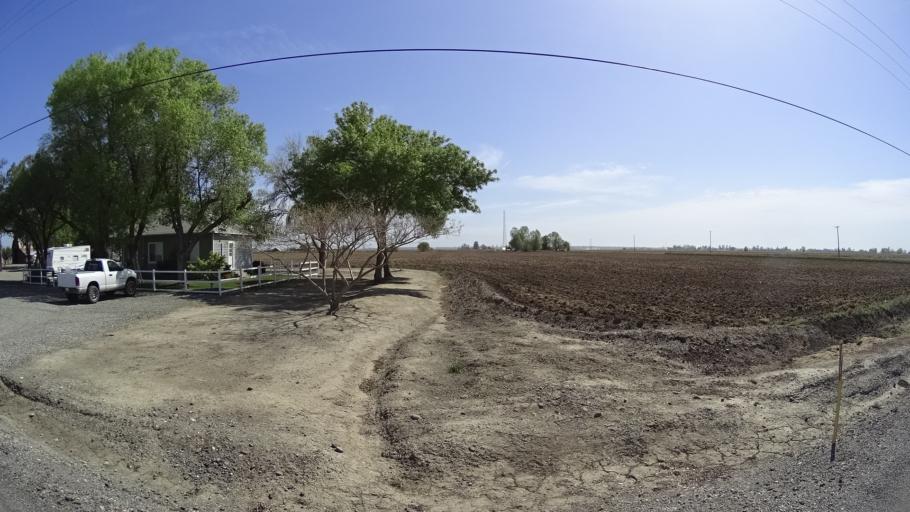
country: US
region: California
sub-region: Glenn County
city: Hamilton City
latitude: 39.5953
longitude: -122.0557
